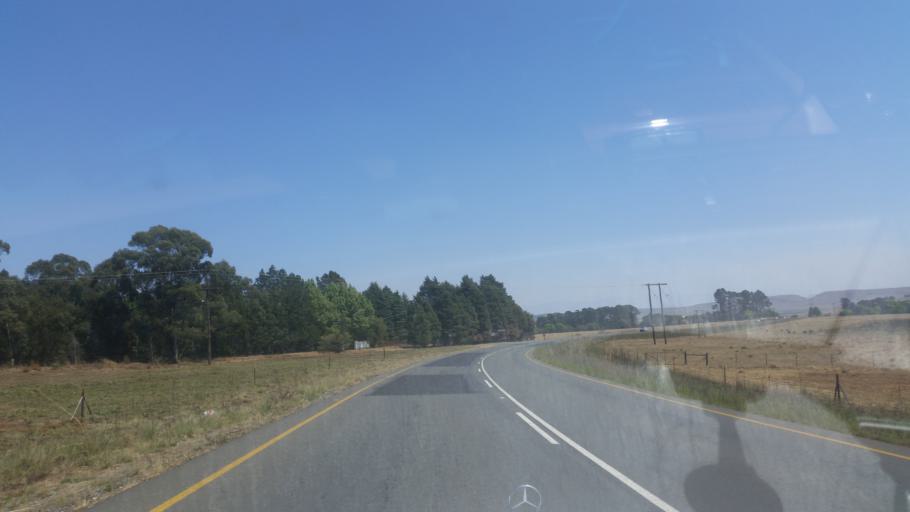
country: ZA
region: KwaZulu-Natal
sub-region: uMgungundlovu District Municipality
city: Mooirivier
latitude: -29.1491
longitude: 29.9852
